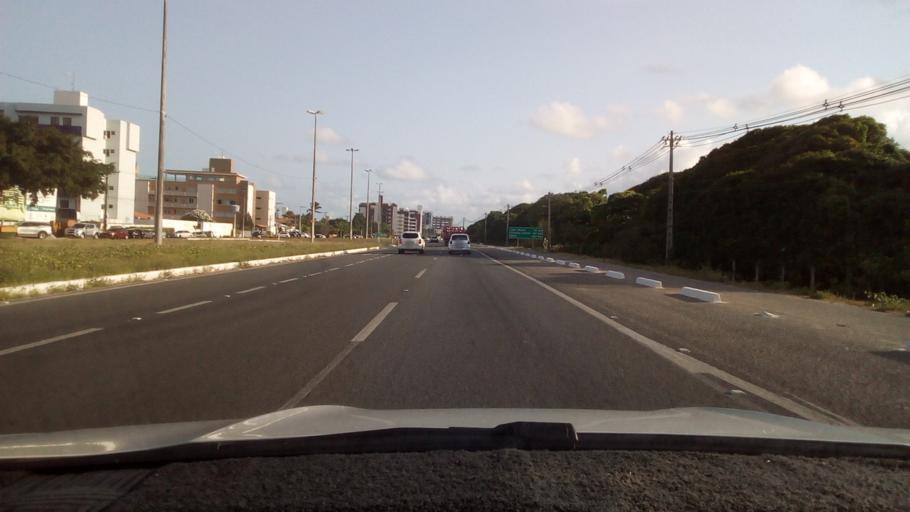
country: BR
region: Paraiba
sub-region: Cabedelo
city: Cabedelo
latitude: -6.9909
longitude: -34.8287
